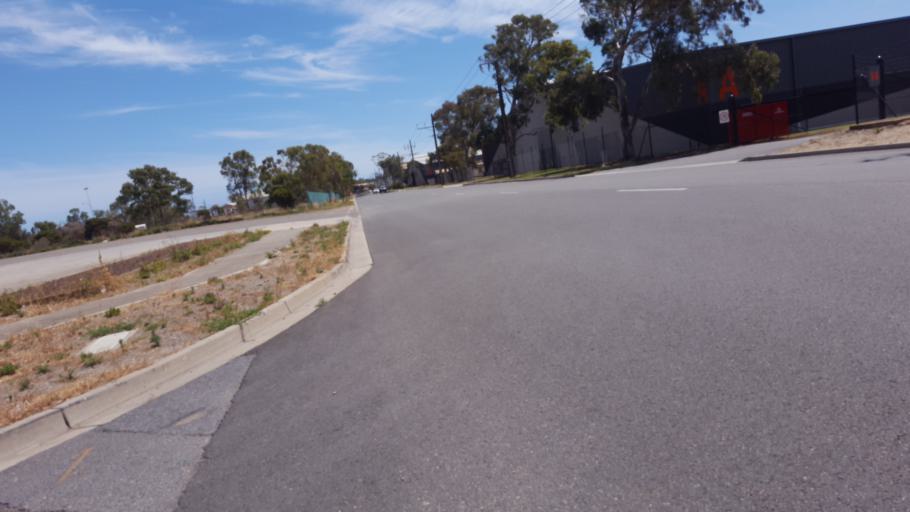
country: AU
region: South Australia
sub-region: Port Adelaide Enfield
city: Alberton
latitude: -34.8426
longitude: 138.5250
